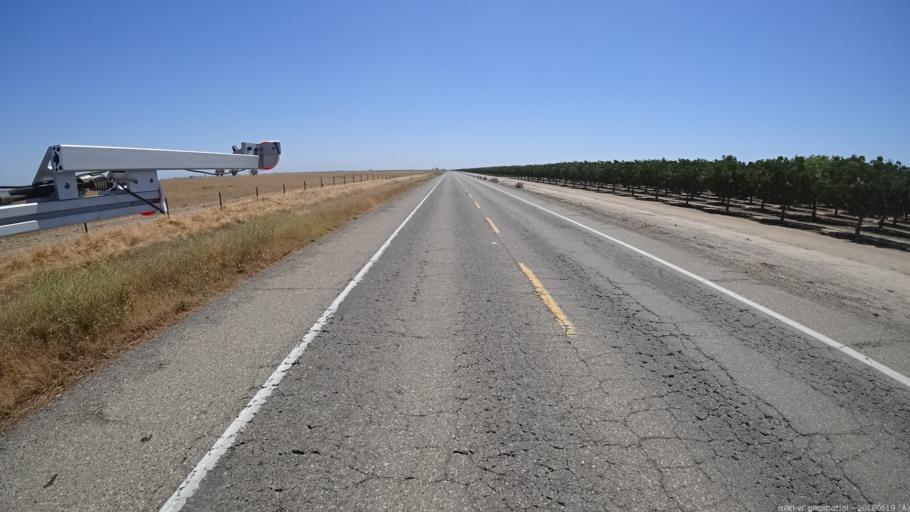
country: US
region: California
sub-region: Fresno County
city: Mendota
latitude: 36.8510
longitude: -120.2521
